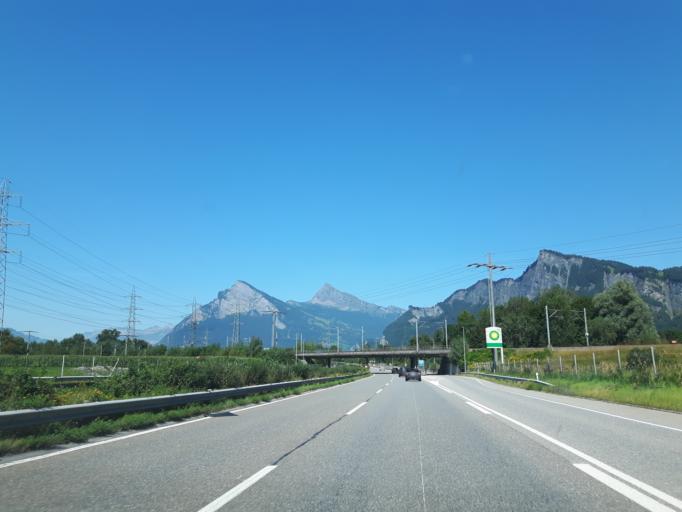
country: CH
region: Saint Gallen
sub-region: Wahlkreis Sarganserland
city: Bad Ragaz
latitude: 47.0086
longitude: 9.5160
